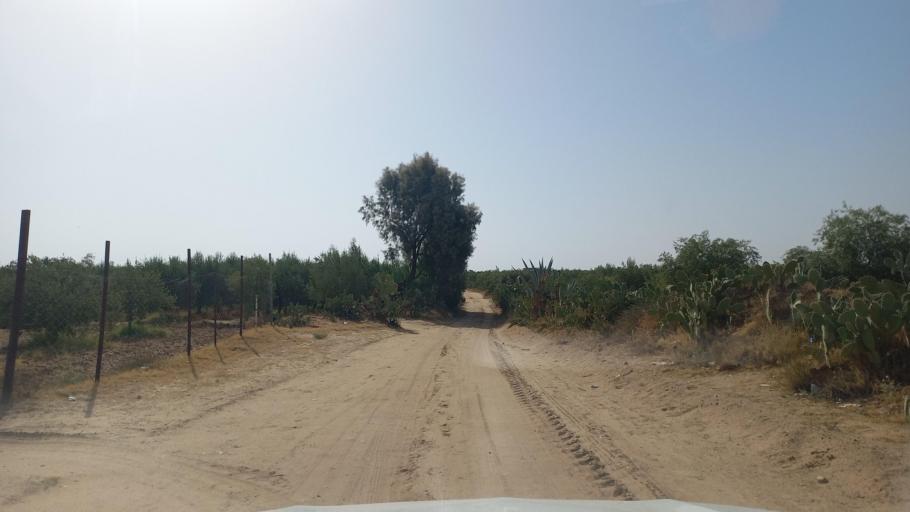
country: TN
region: Al Qasrayn
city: Kasserine
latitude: 35.2510
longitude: 9.0302
